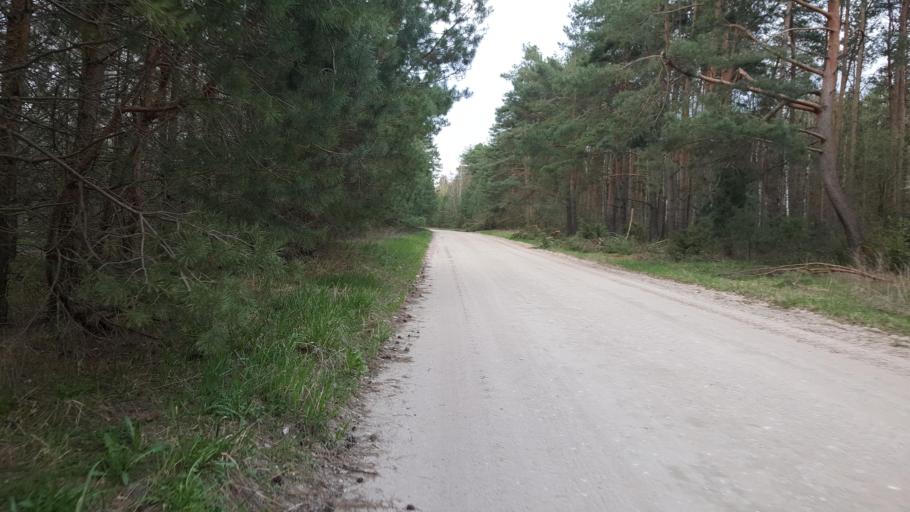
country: BY
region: Brest
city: Kamyanyets
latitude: 52.3977
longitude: 23.7401
